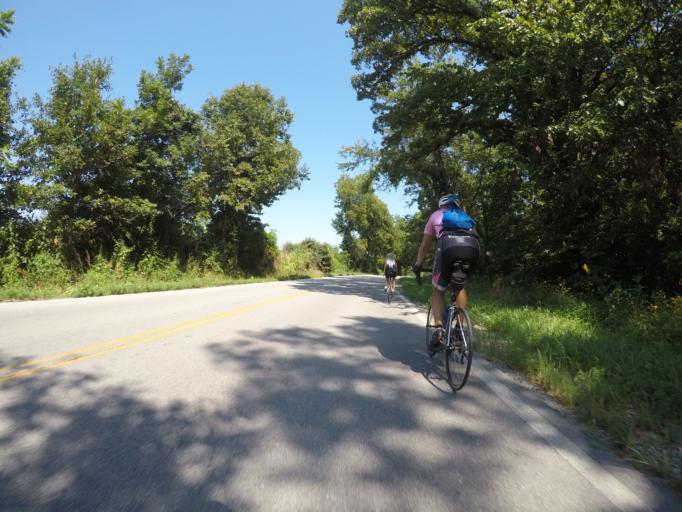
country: US
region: Kansas
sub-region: Leavenworth County
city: Lansing
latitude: 39.2162
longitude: -94.8470
